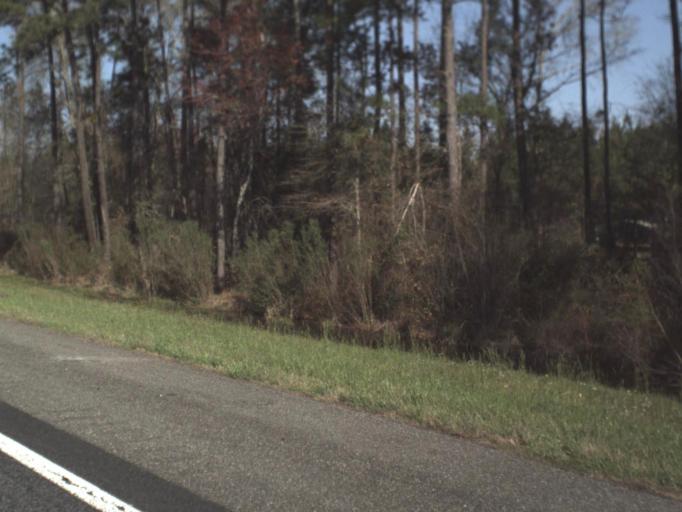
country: US
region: Florida
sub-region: Gadsden County
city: Midway
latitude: 30.4875
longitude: -84.4177
